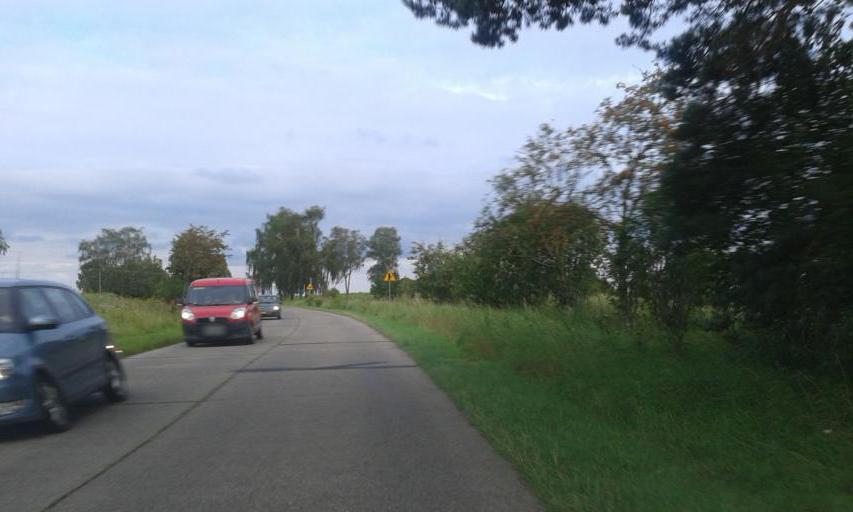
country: PL
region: West Pomeranian Voivodeship
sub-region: Powiat szczecinecki
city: Lubowo
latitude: 53.5842
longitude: 16.4416
